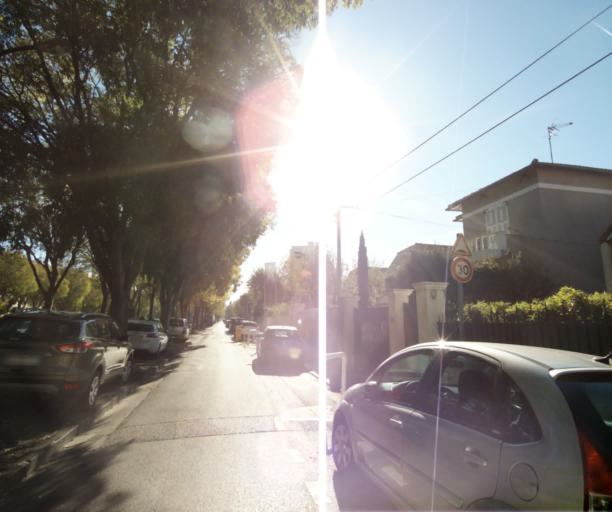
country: FR
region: Provence-Alpes-Cote d'Azur
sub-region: Departement des Bouches-du-Rhone
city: Marseille 09
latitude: 43.2643
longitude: 5.3957
